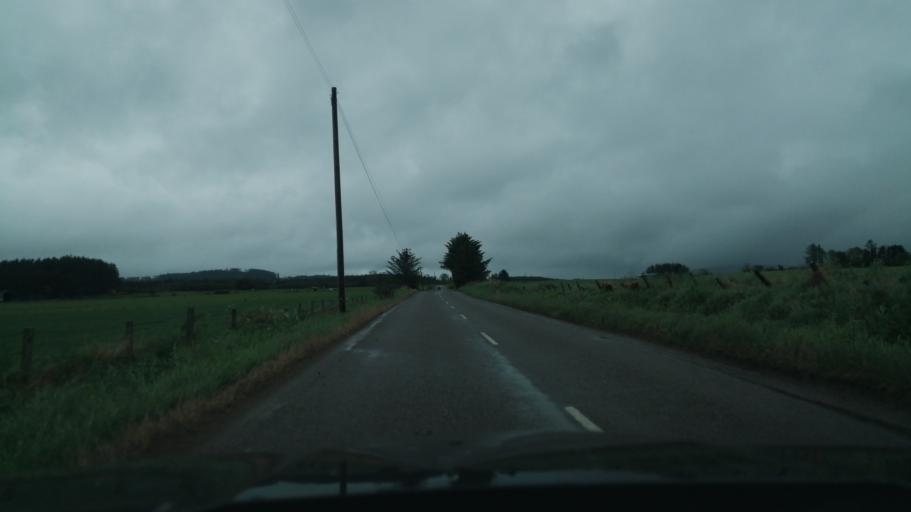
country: GB
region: Scotland
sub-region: Aberdeenshire
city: Huntly
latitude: 57.5399
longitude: -2.7832
